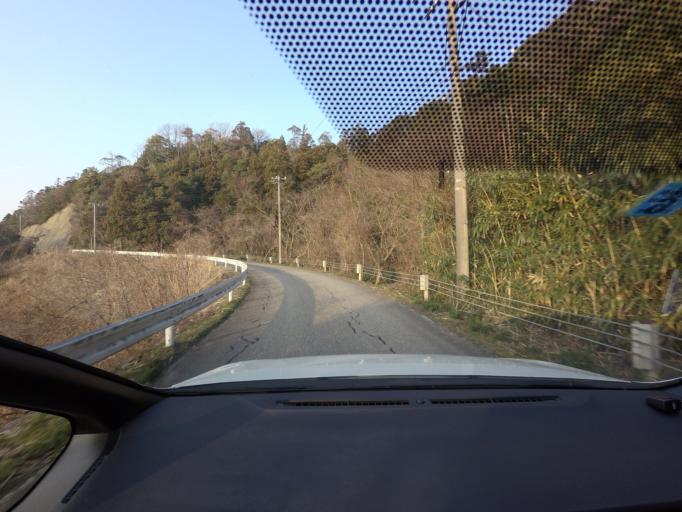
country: JP
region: Ishikawa
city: Nanao
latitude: 37.1445
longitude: 137.0246
